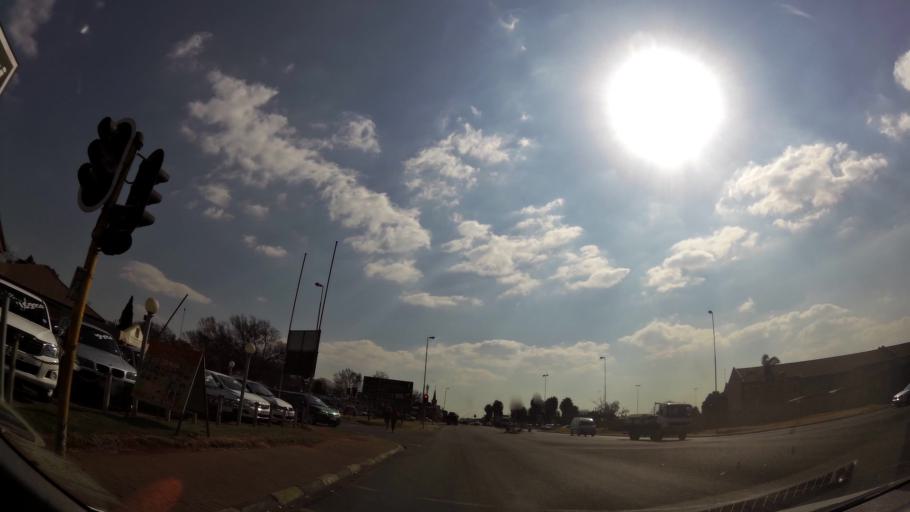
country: ZA
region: Gauteng
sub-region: Ekurhuleni Metropolitan Municipality
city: Boksburg
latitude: -26.2007
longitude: 28.2453
